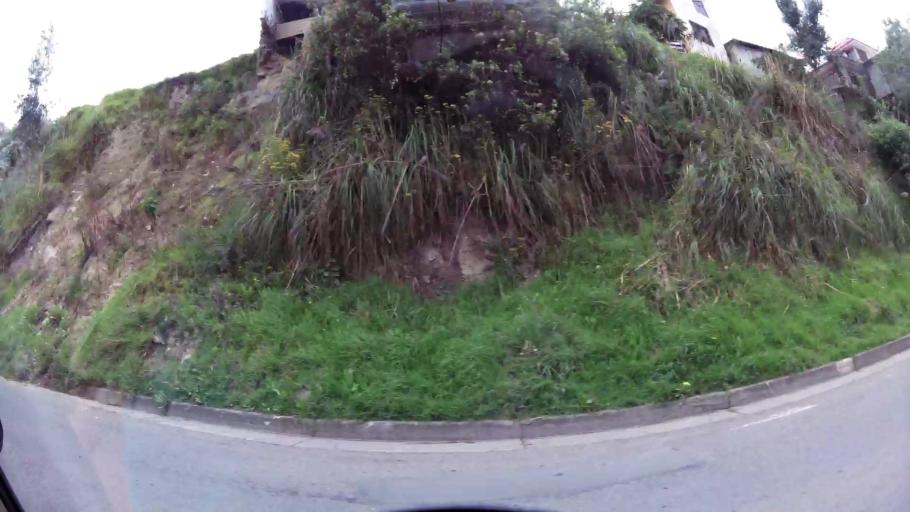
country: EC
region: Azuay
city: Cuenca
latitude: -2.8984
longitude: -79.0519
